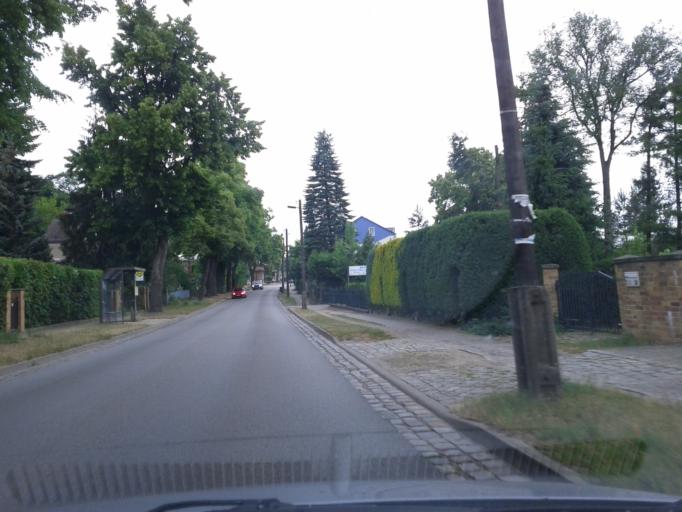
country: DE
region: Brandenburg
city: Woltersdorf
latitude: 52.4444
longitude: 13.7568
